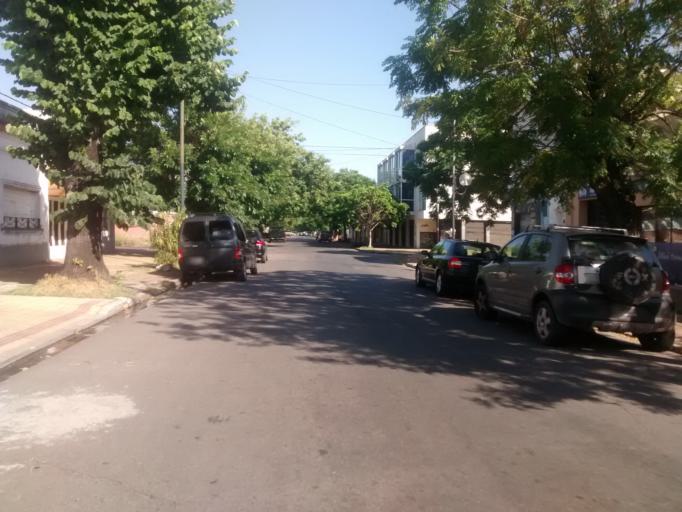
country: AR
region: Buenos Aires
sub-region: Partido de La Plata
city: La Plata
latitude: -34.9302
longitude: -57.9359
